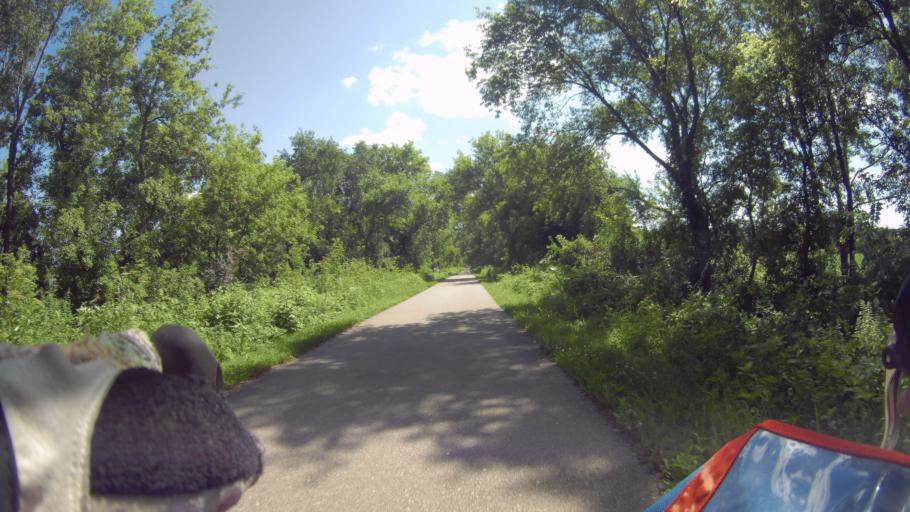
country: US
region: Wisconsin
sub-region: Dane County
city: Fitchburg
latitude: 42.9467
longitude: -89.4785
